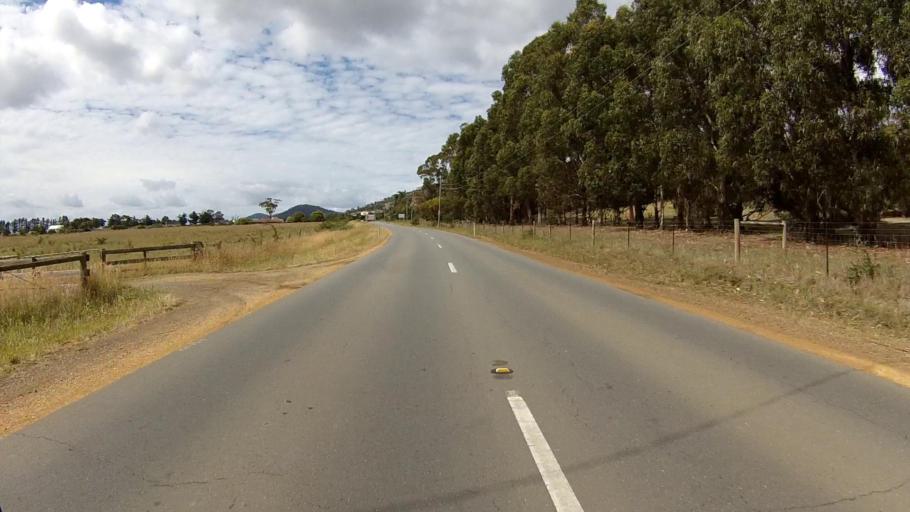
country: AU
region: Tasmania
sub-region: Clarence
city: Cambridge
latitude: -42.7851
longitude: 147.4159
